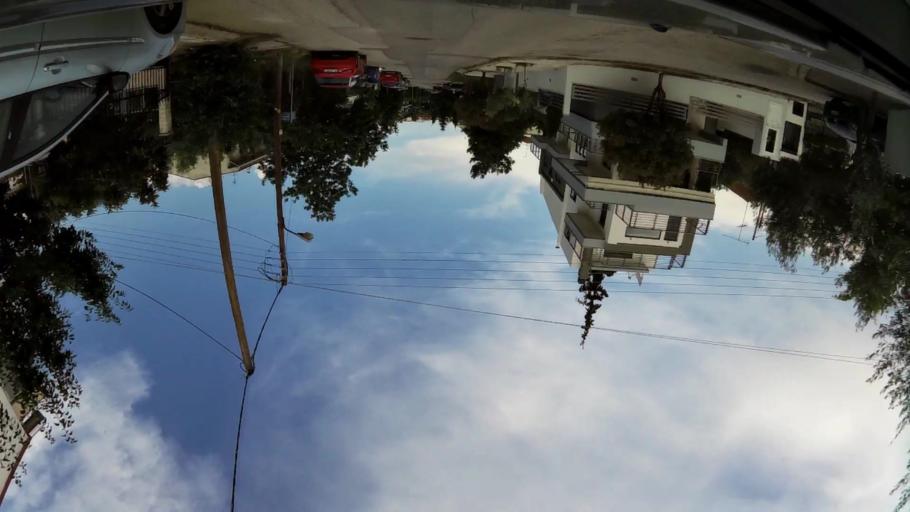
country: GR
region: Central Macedonia
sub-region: Nomos Thessalonikis
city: Pefka
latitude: 40.6604
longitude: 22.9871
